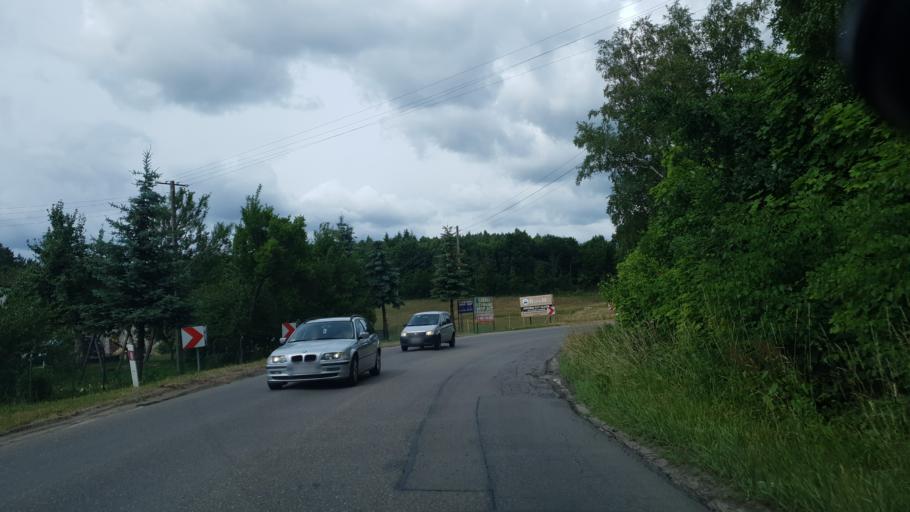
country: PL
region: Pomeranian Voivodeship
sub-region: Powiat kartuski
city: Przodkowo
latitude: 54.3593
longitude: 18.2430
